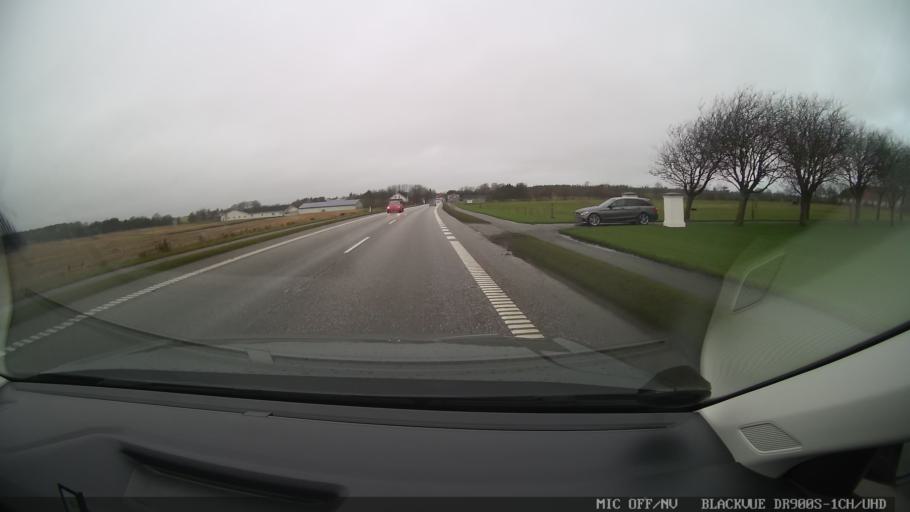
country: DK
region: Central Jutland
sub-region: Viborg Kommune
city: Karup
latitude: 56.3268
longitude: 9.2642
